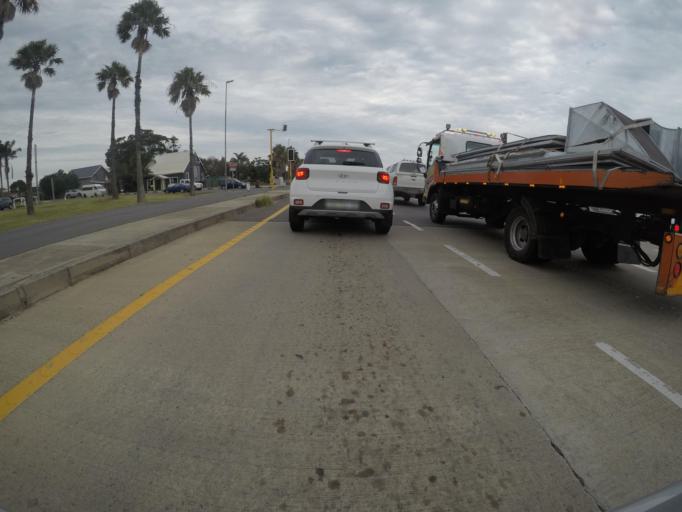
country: ZA
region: Eastern Cape
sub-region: Buffalo City Metropolitan Municipality
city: East London
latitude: -32.9349
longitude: 27.9926
